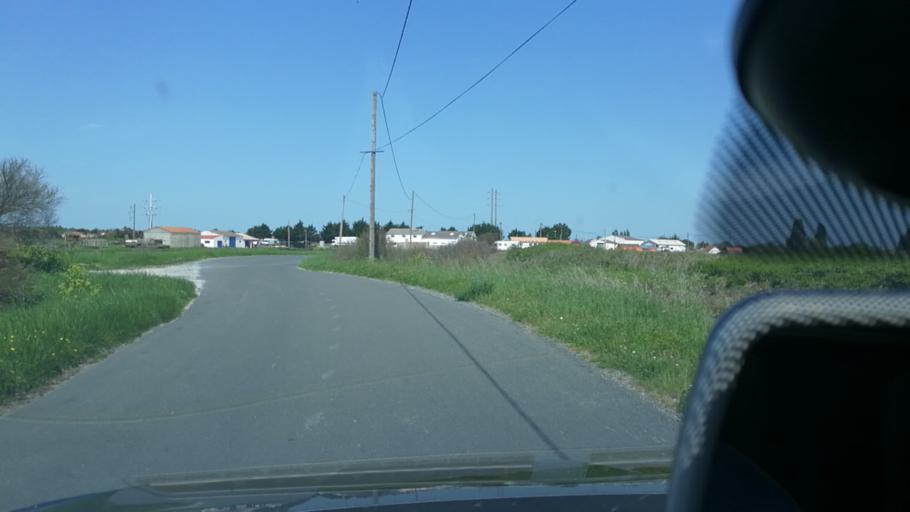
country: FR
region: Poitou-Charentes
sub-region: Departement de la Charente-Maritime
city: Saint-Trojan-les-Bains
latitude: 45.8684
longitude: -1.2200
